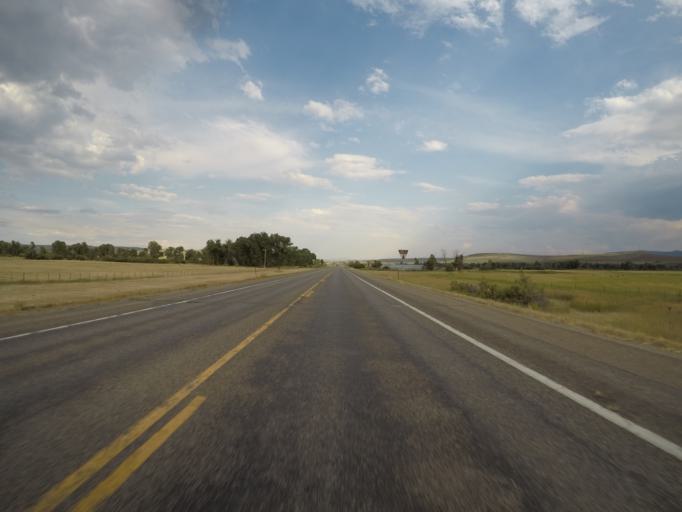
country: US
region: Colorado
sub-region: Moffat County
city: Craig
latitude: 40.5323
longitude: -107.4380
